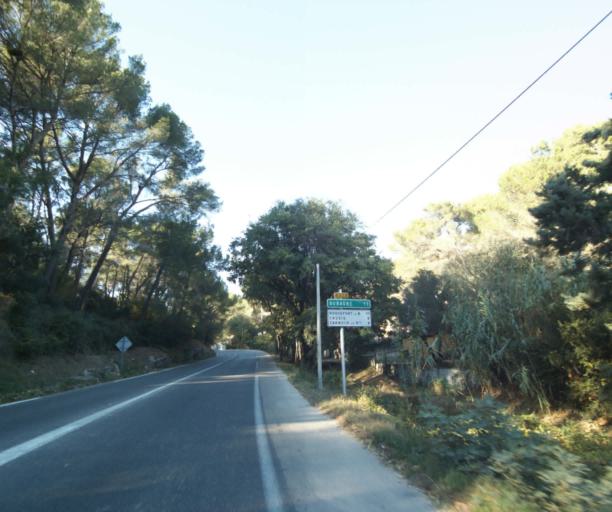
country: FR
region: Provence-Alpes-Cote d'Azur
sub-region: Departement des Bouches-du-Rhone
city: La Ciotat
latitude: 43.1952
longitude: 5.5983
